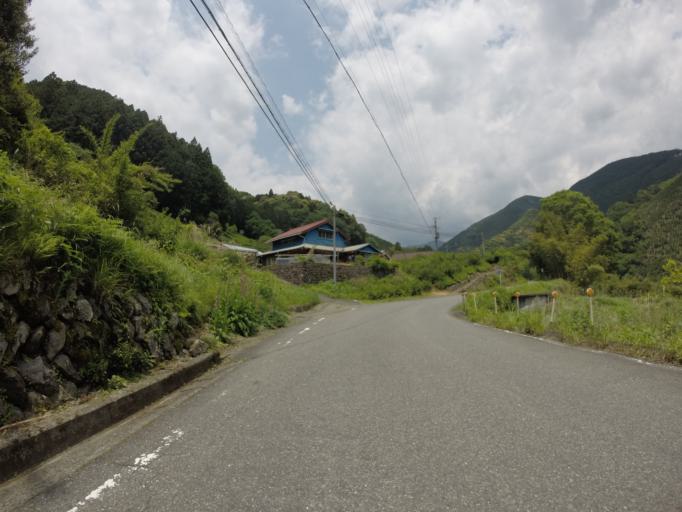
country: JP
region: Shizuoka
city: Shizuoka-shi
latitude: 35.1254
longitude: 138.3002
